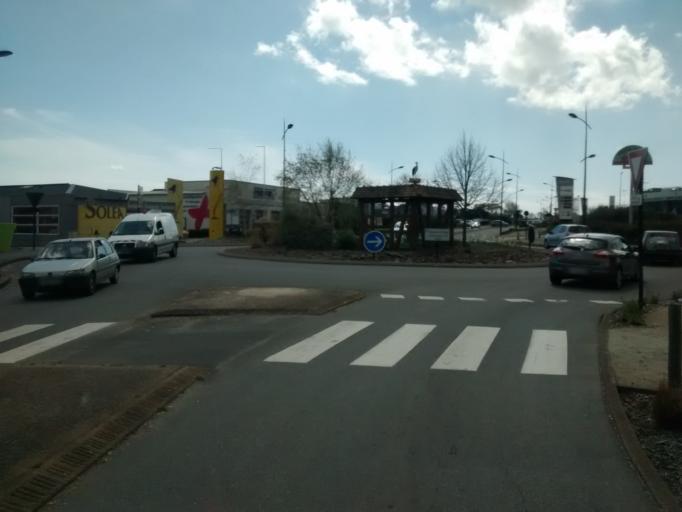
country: FR
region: Brittany
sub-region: Departement du Morbihan
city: Vannes
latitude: 47.6531
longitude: -2.7210
